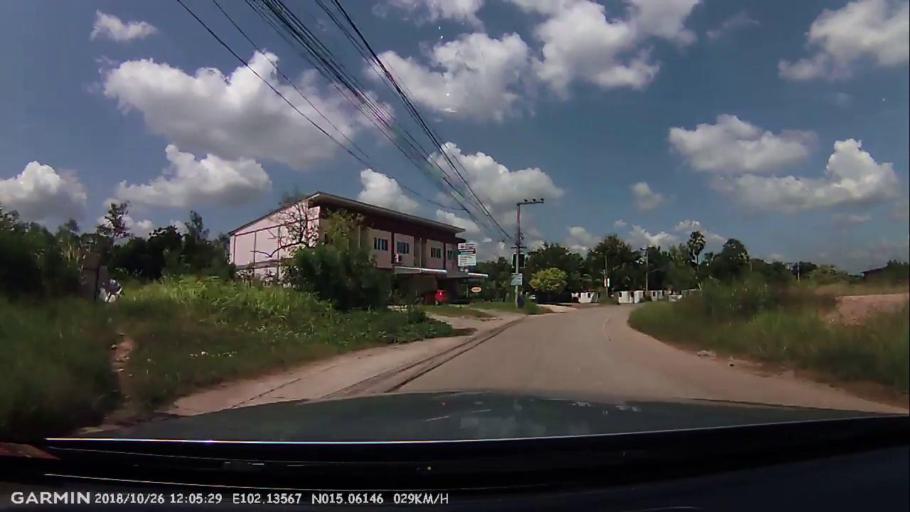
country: TH
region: Nakhon Ratchasima
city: Nakhon Ratchasima
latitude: 15.0615
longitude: 102.1357
